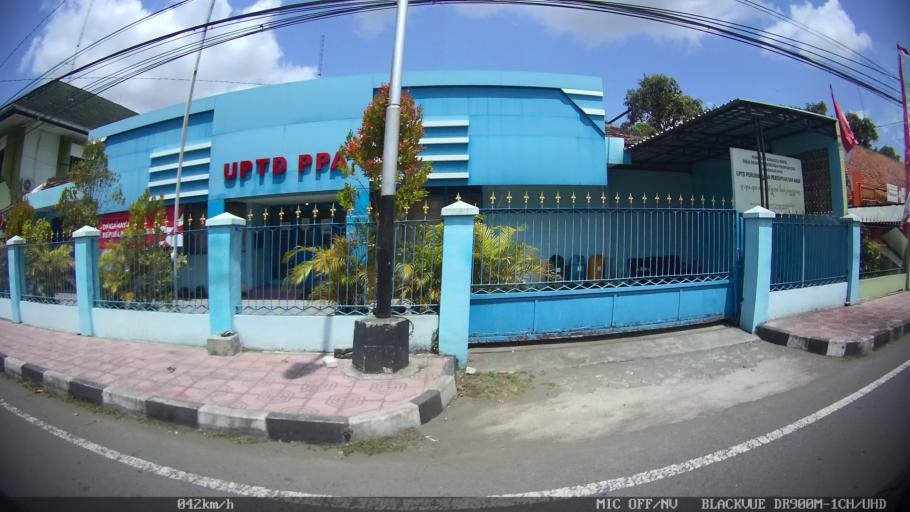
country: ID
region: Daerah Istimewa Yogyakarta
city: Bantul
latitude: -7.8931
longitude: 110.3370
